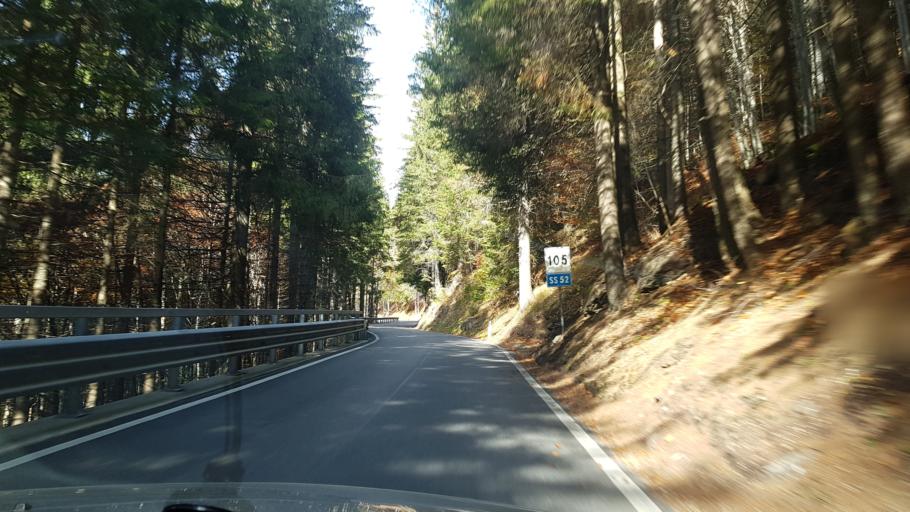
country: IT
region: Veneto
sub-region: Provincia di Belluno
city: Candide
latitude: 46.6406
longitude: 12.4567
